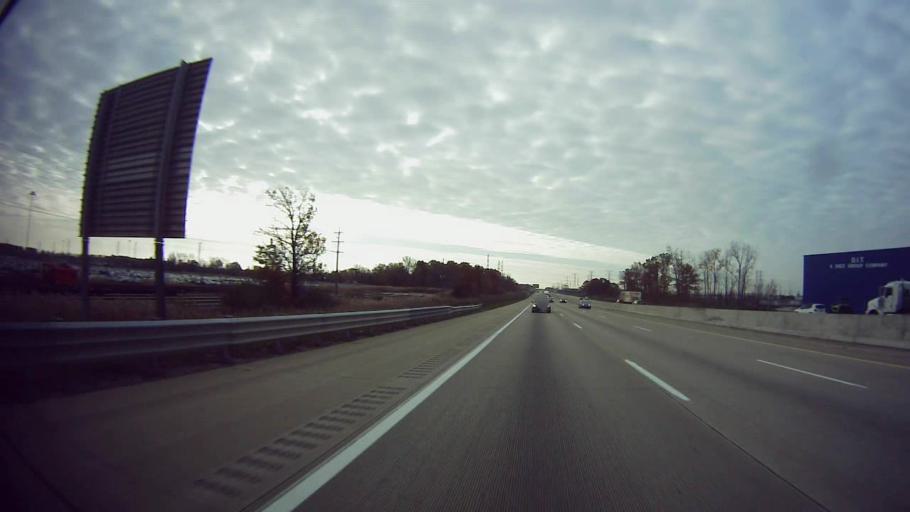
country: US
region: Michigan
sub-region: Wayne County
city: Woodhaven
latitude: 42.1171
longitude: -83.2414
